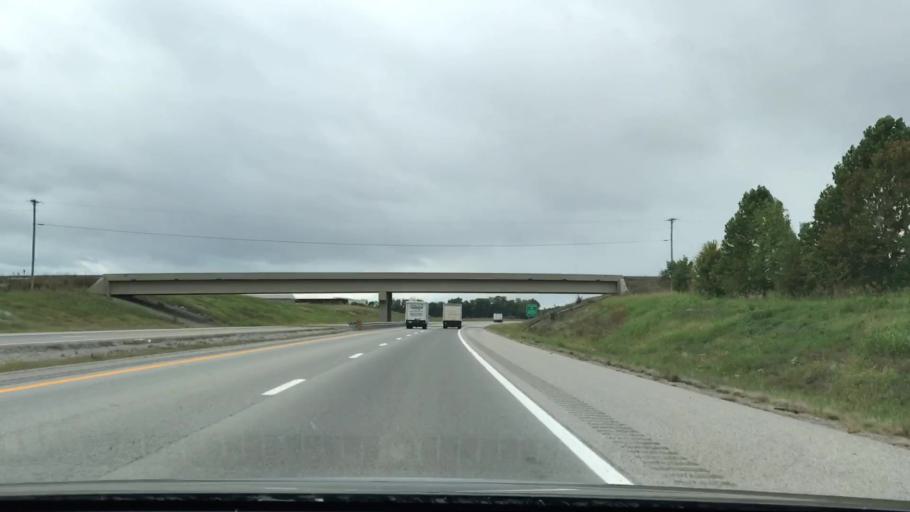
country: US
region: Kentucky
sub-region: Christian County
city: Hopkinsville
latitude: 36.7647
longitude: -87.5007
